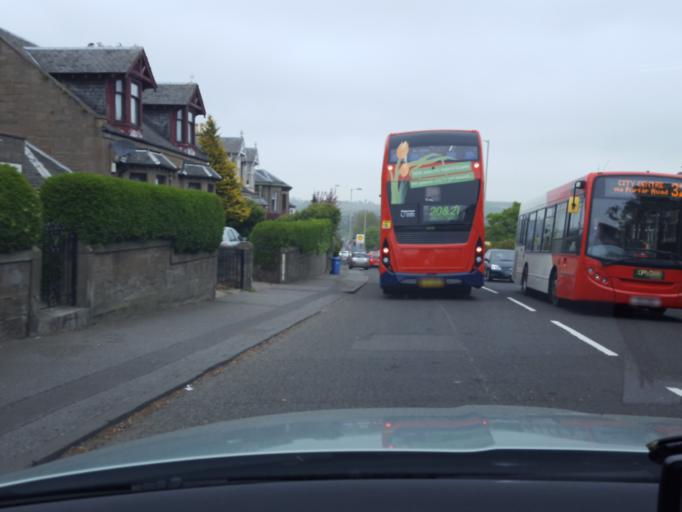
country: GB
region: Scotland
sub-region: Dundee City
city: Dundee
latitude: 56.4789
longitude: -2.9526
